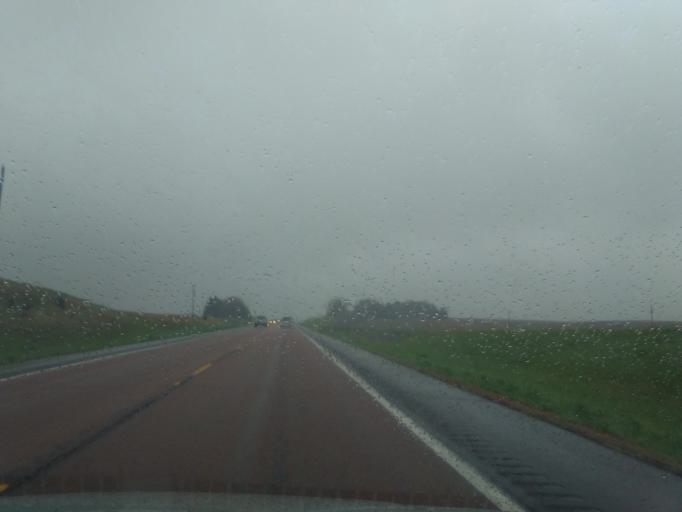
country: US
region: Nebraska
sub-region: Wayne County
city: Wayne
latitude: 42.2355
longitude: -97.1509
